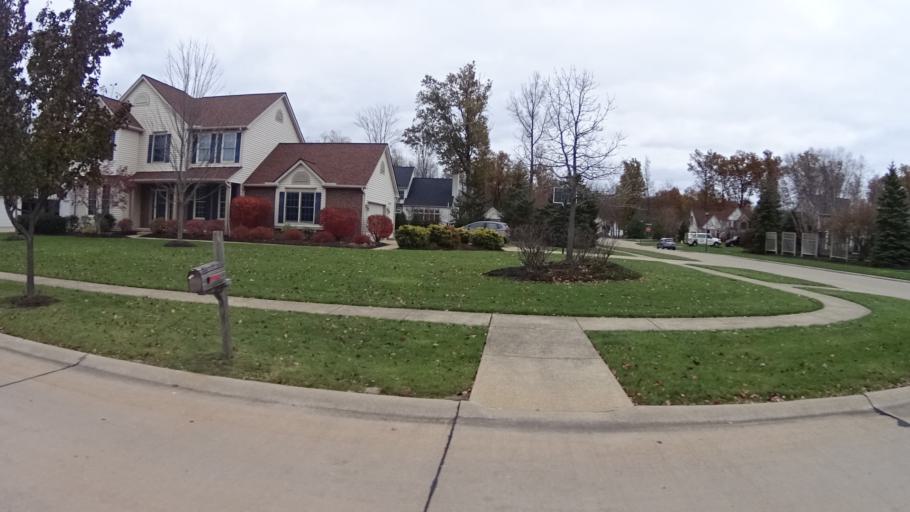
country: US
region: Ohio
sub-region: Lorain County
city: Avon Center
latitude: 41.4865
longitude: -81.9786
